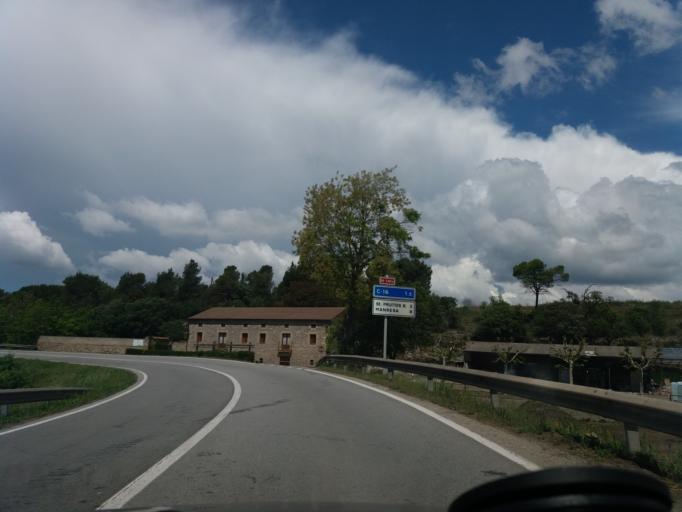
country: ES
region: Catalonia
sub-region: Provincia de Barcelona
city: Navarcles
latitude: 41.7605
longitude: 1.9008
